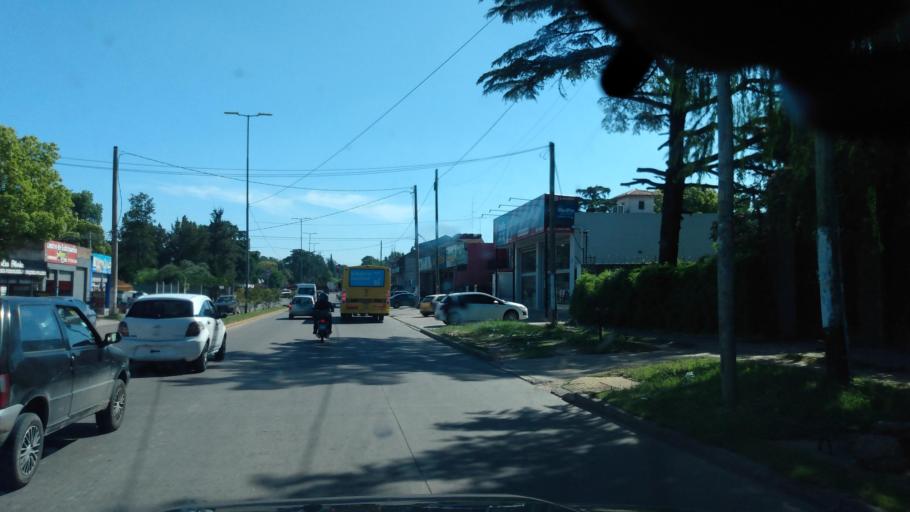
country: AR
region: Buenos Aires
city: Hurlingham
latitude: -34.5548
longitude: -58.7254
